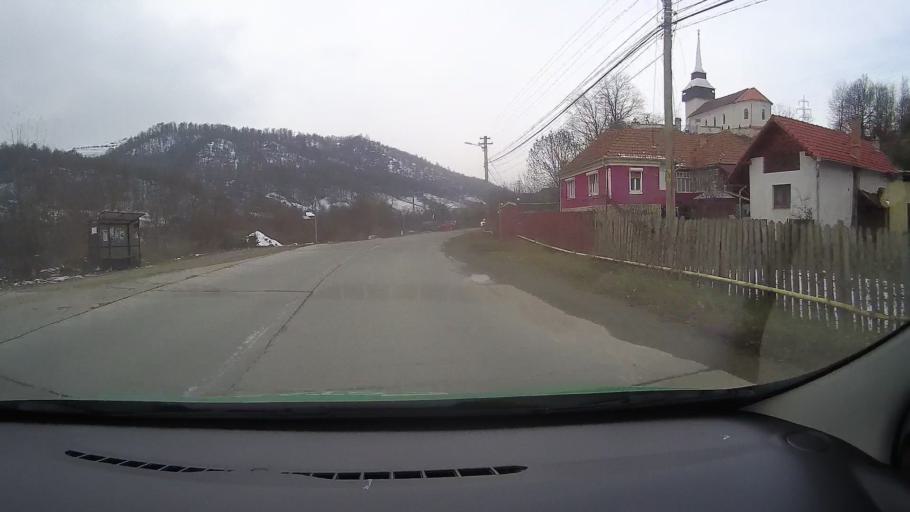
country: RO
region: Alba
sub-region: Oras Zlatna
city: Zlatna
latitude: 46.0913
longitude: 23.2597
